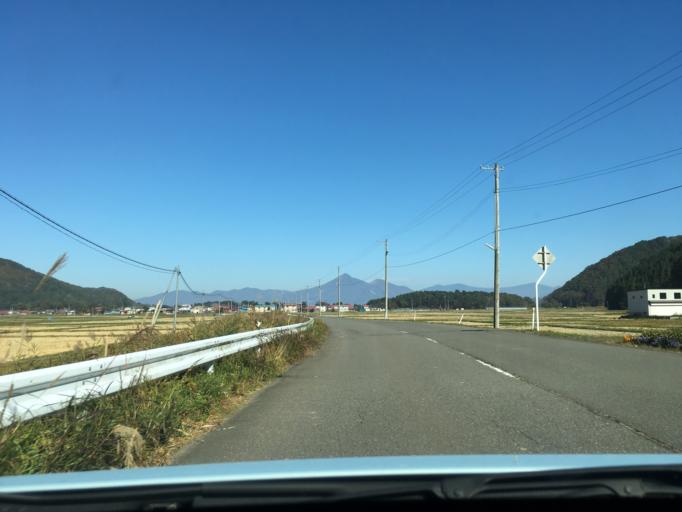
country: JP
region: Fukushima
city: Inawashiro
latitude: 37.4098
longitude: 140.0858
